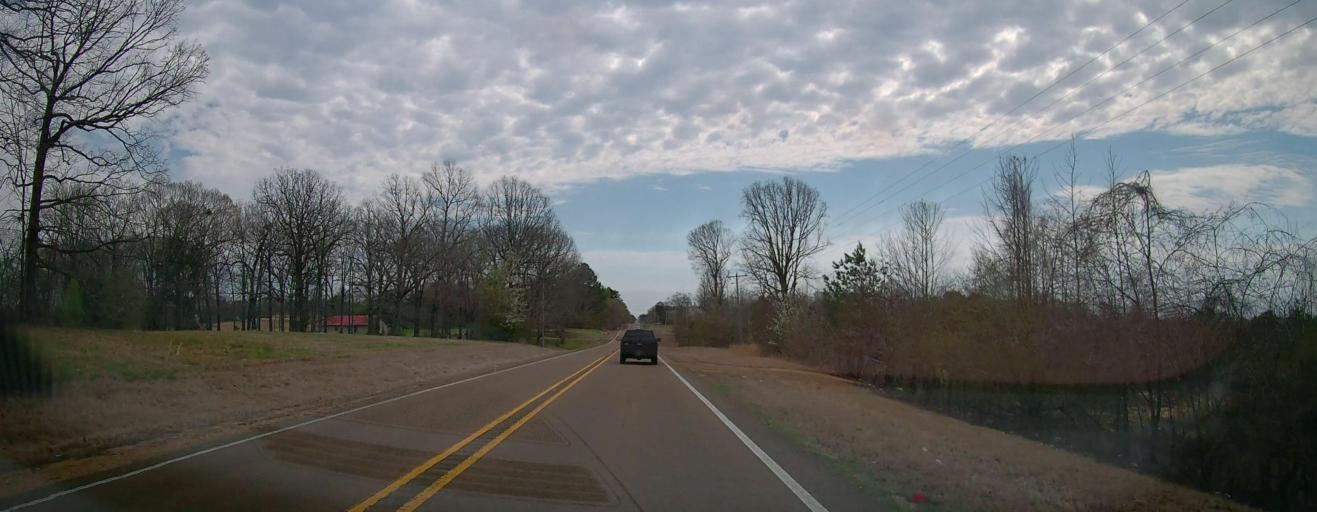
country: US
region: Mississippi
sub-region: Marshall County
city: Byhalia
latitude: 34.8349
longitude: -89.5846
